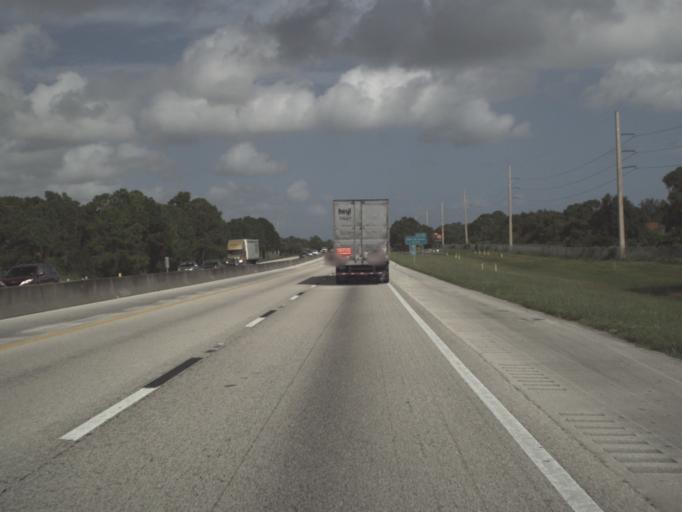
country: US
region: Florida
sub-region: Saint Lucie County
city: Port Saint Lucie
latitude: 27.2440
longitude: -80.3460
